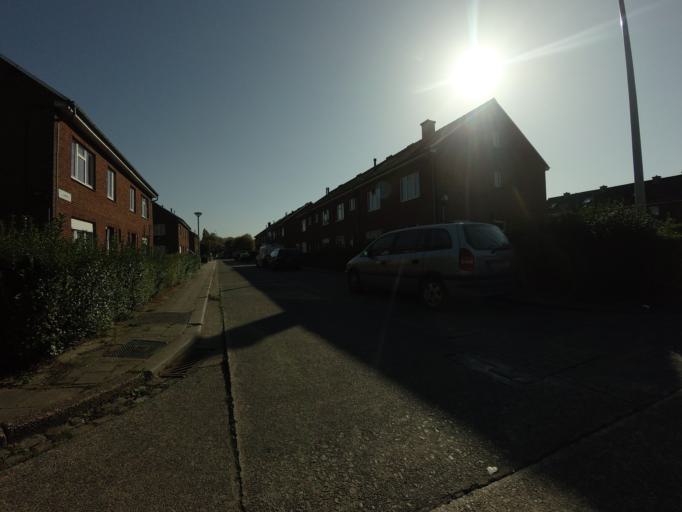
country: BE
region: Flanders
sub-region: Provincie Antwerpen
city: Duffel
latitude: 51.0922
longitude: 4.5154
